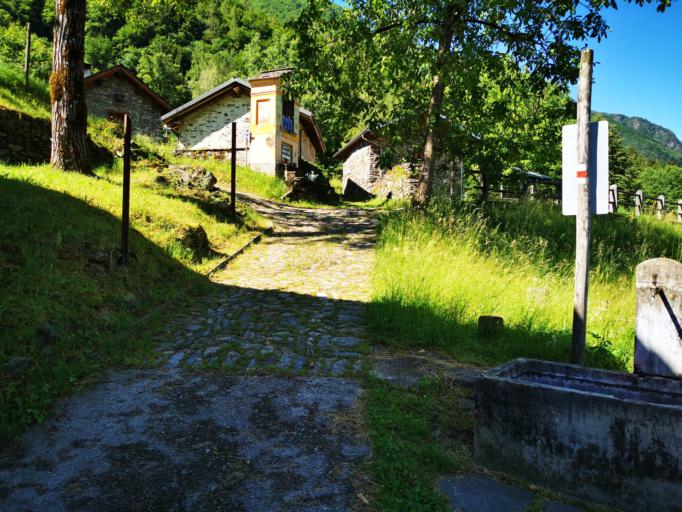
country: CH
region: Grisons
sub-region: Moesa District
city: Roveredo
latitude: 46.2294
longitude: 9.1194
